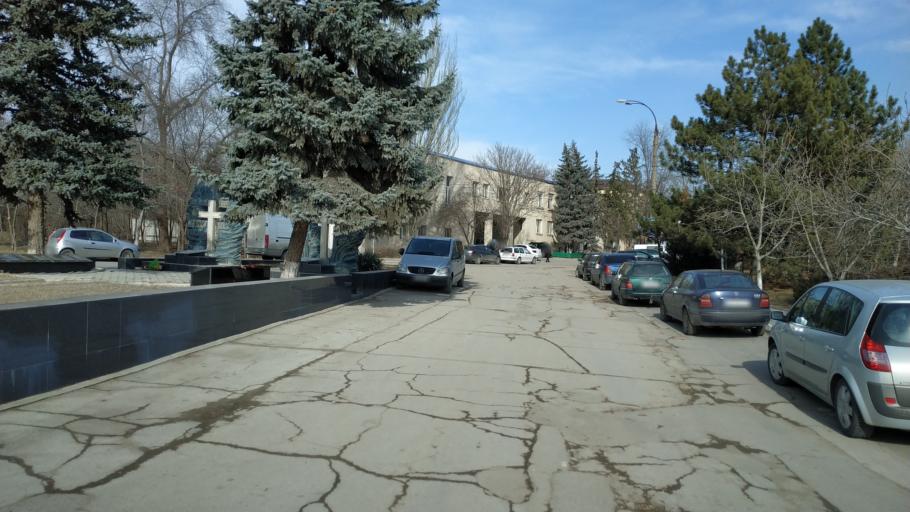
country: MD
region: Nisporeni
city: Nisporeni
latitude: 47.0792
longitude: 28.1883
